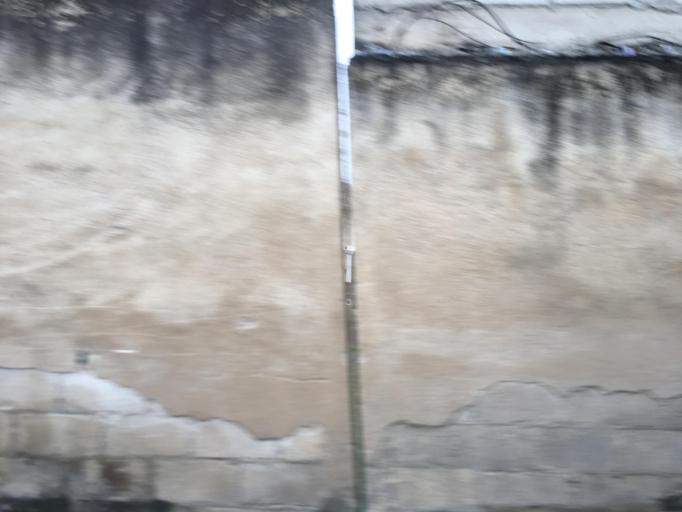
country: GT
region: Sacatepequez
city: Jocotenango
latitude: 14.5763
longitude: -90.7458
